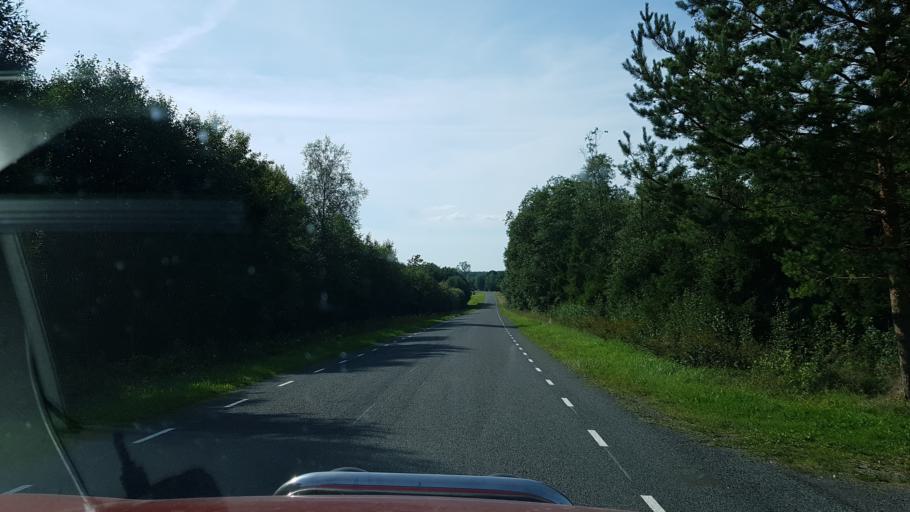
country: EE
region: Viljandimaa
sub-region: Abja vald
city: Abja-Paluoja
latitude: 58.3380
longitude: 25.2515
